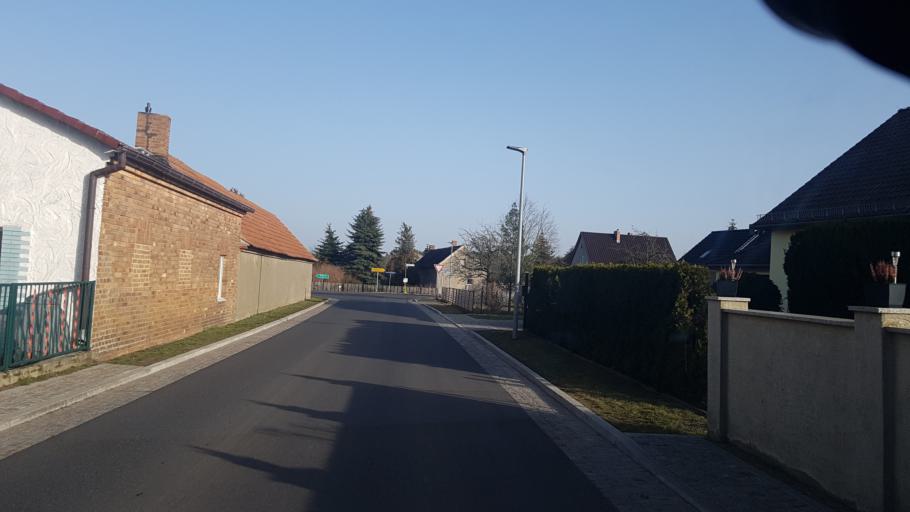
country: DE
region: Brandenburg
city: Heinersbruck
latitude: 51.7019
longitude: 14.4614
